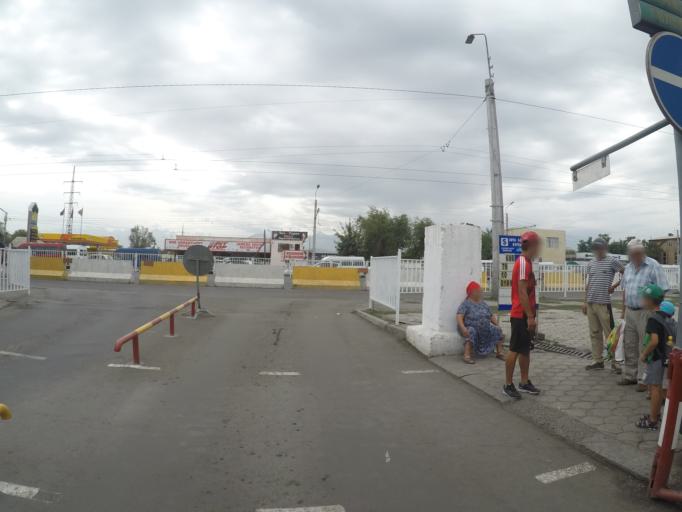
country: KG
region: Chuy
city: Bishkek
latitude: 42.8854
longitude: 74.5663
